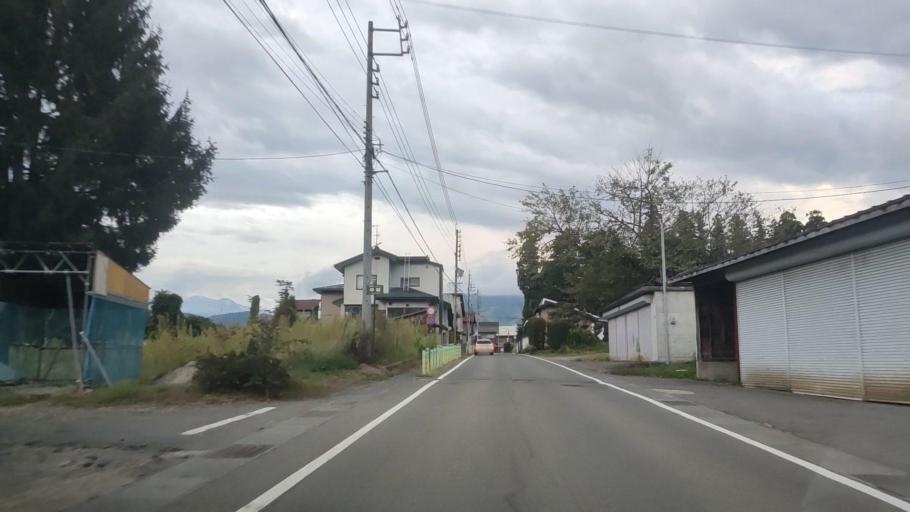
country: JP
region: Nagano
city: Iiyama
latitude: 36.8689
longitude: 138.4075
